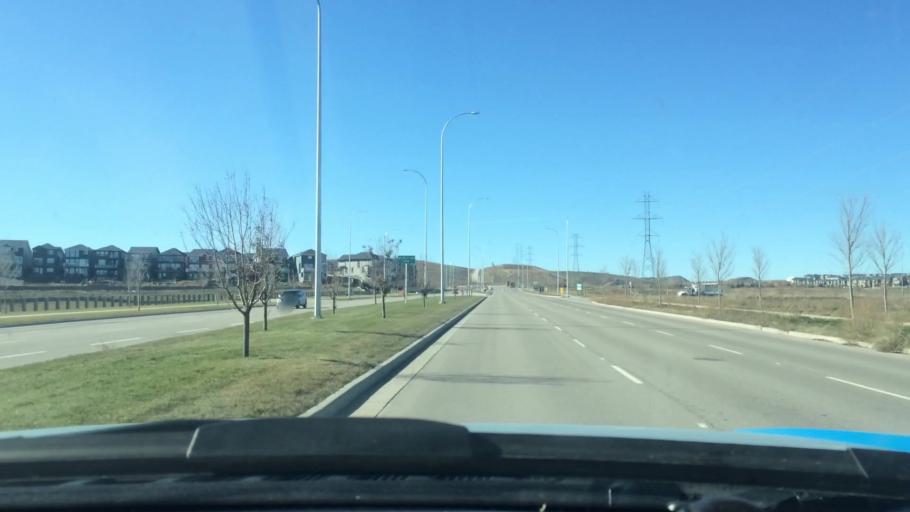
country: CA
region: Alberta
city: Calgary
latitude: 51.1681
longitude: -114.1539
